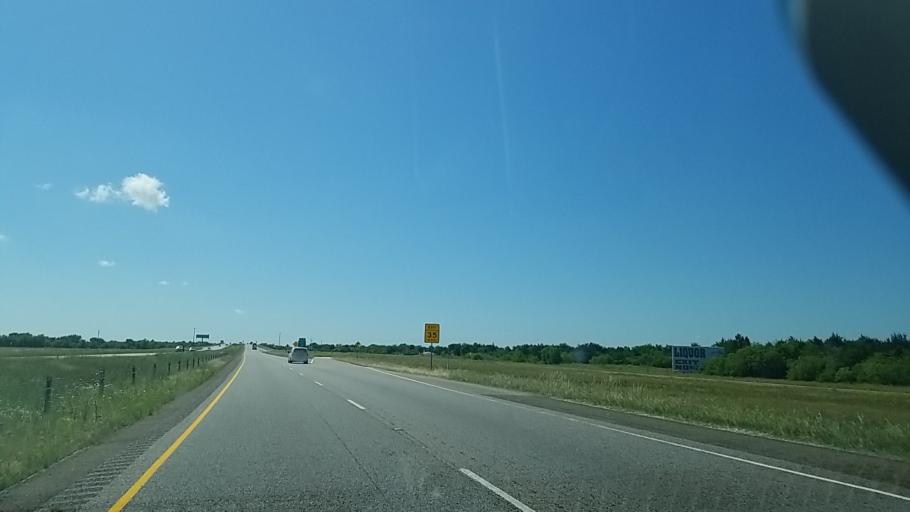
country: US
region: Texas
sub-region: Freestone County
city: Wortham
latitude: 31.8615
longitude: -96.3128
